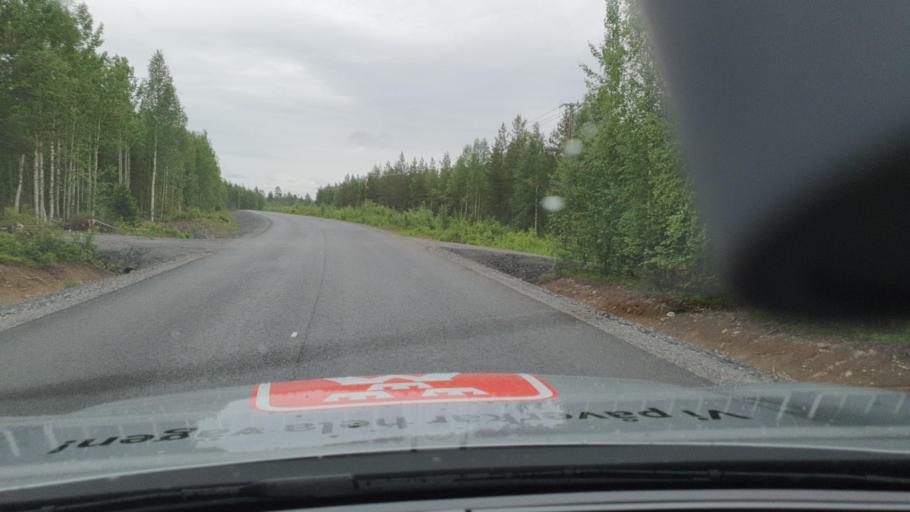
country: SE
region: Norrbotten
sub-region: Overkalix Kommun
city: OEverkalix
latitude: 66.7227
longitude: 23.1845
